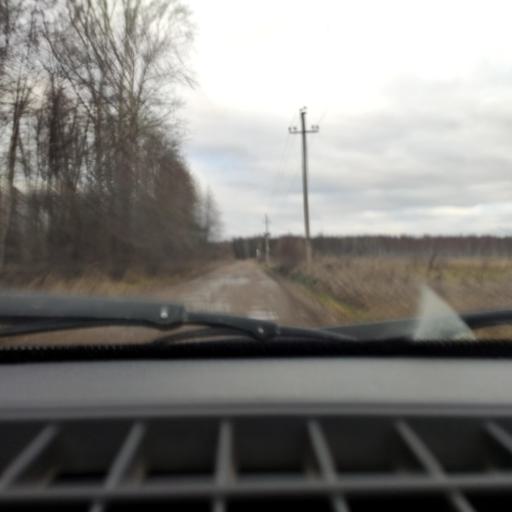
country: RU
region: Bashkortostan
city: Avdon
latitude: 54.6308
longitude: 55.7339
